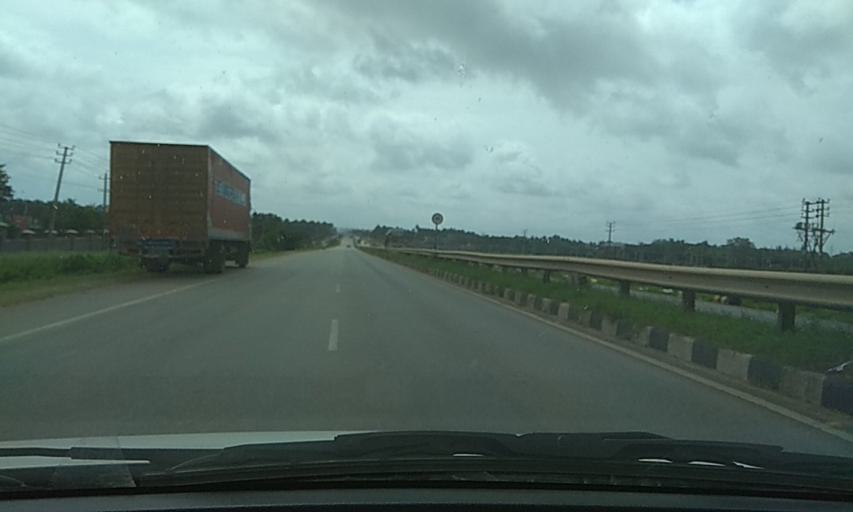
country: IN
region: Karnataka
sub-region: Davanagere
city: Harihar
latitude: 14.4542
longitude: 75.8700
